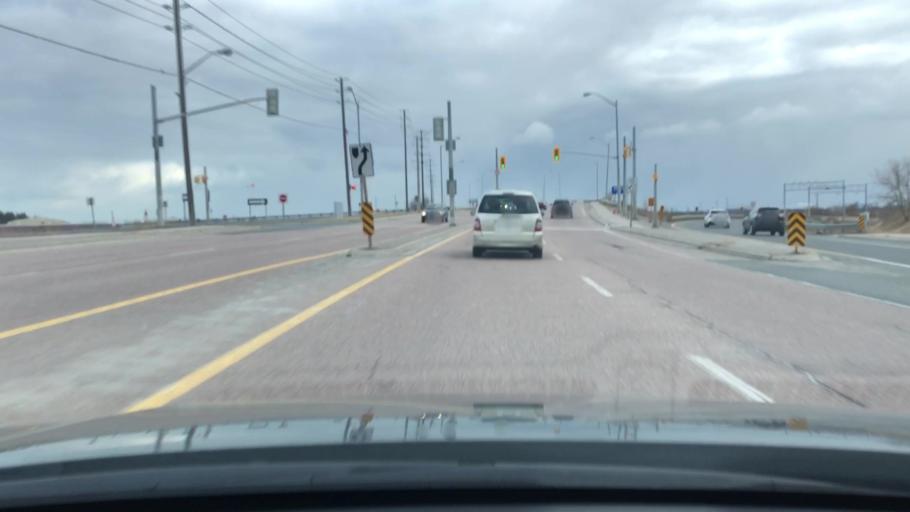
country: CA
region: Ontario
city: Markham
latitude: 43.8729
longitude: -79.2335
